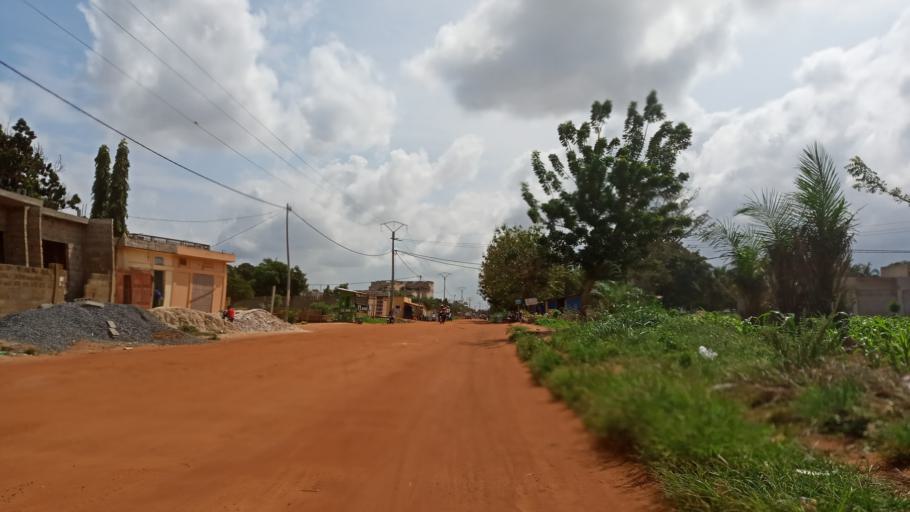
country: TG
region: Maritime
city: Lome
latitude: 6.2330
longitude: 1.1359
